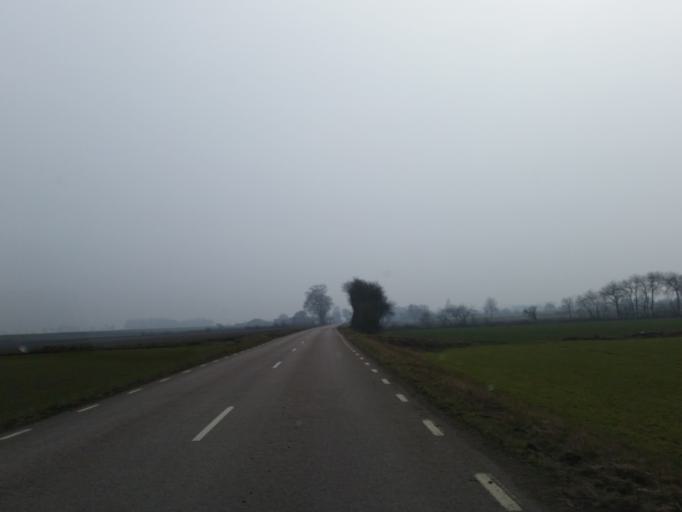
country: SE
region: Kalmar
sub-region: Morbylanga Kommun
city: Moerbylanga
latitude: 56.4001
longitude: 16.4153
